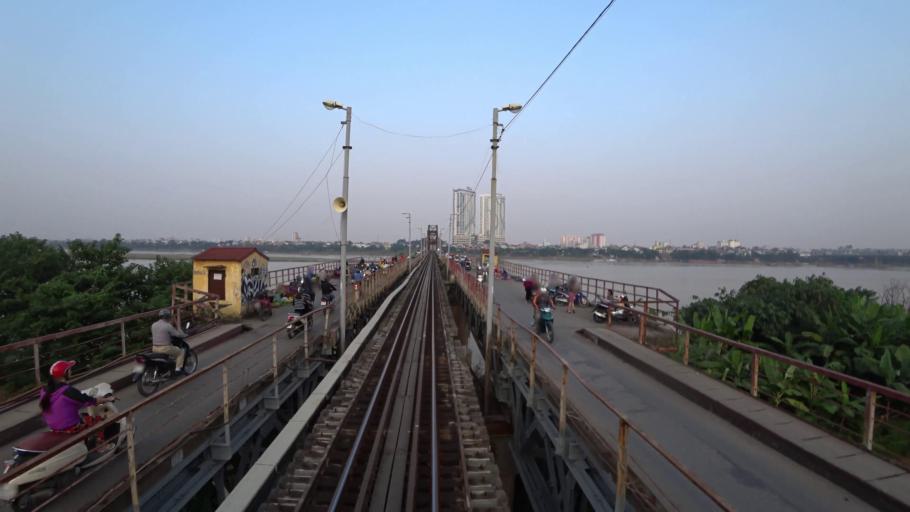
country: VN
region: Ha Noi
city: Hoan Kiem
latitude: 21.0445
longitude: 105.8616
